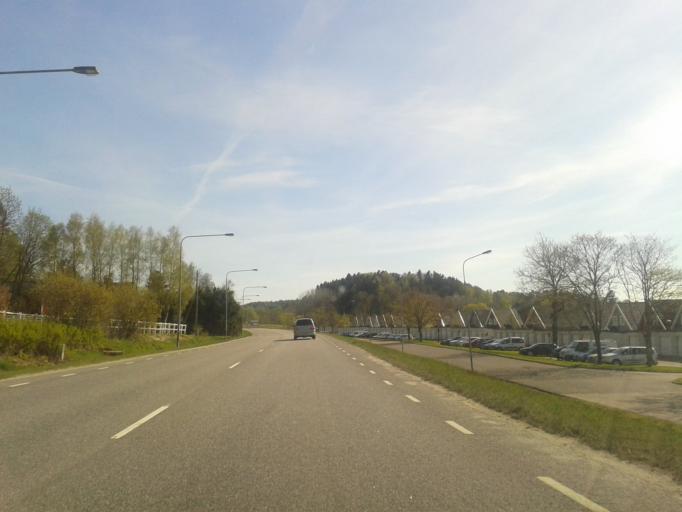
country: SE
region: Vaestra Goetaland
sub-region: Ale Kommun
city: Nodinge-Nol
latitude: 57.8939
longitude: 12.0680
